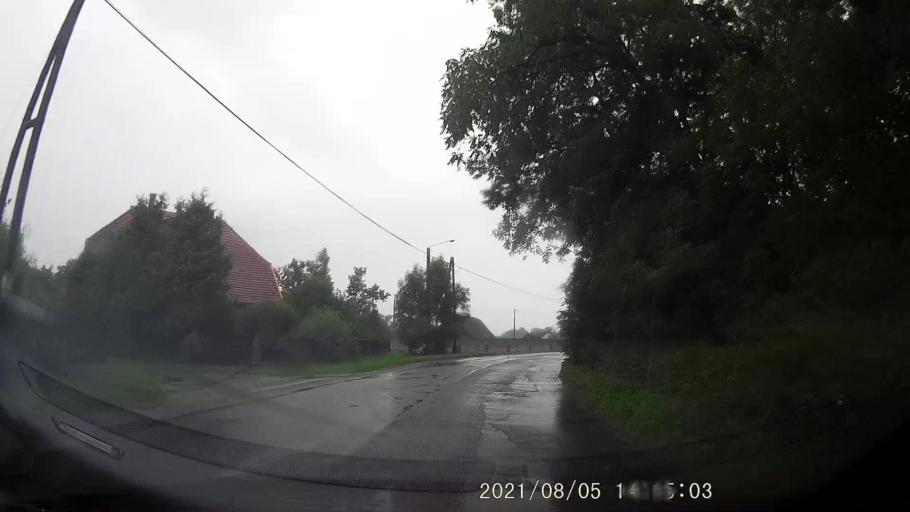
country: PL
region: Opole Voivodeship
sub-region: Powiat prudnicki
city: Biala
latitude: 50.4649
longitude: 17.7380
